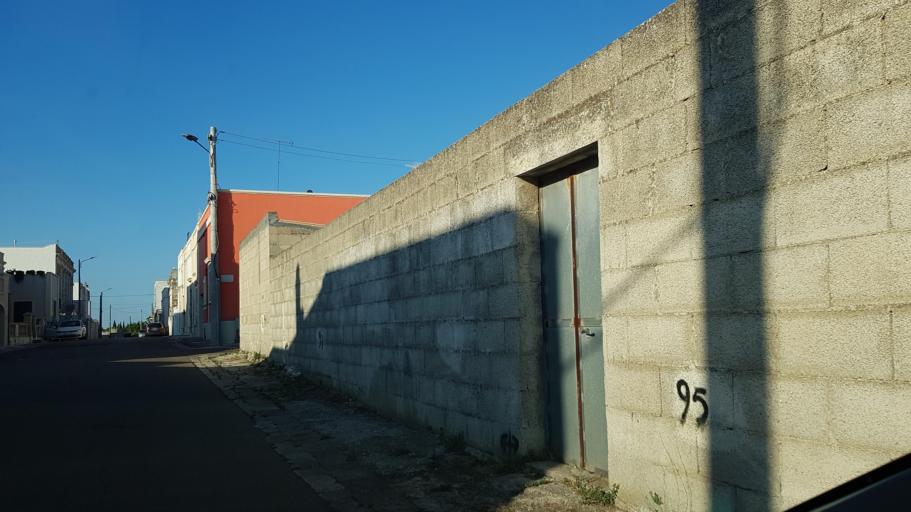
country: IT
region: Apulia
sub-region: Provincia di Lecce
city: Marittima
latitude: 39.9970
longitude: 18.4022
